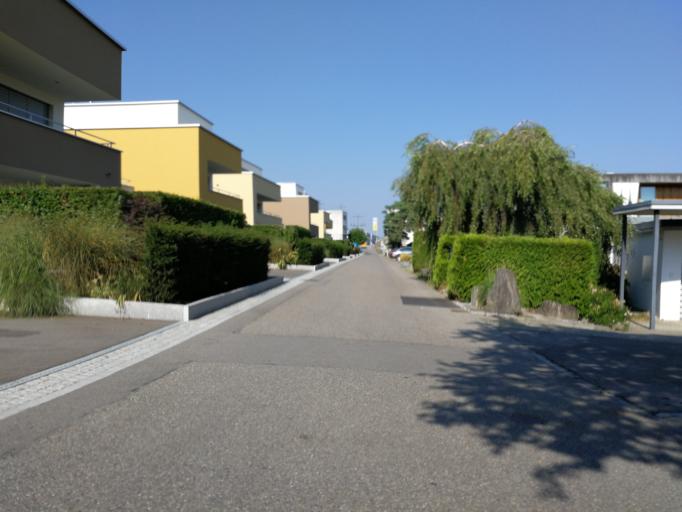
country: CH
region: Schwyz
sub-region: Bezirk March
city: Altendorf
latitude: 47.2024
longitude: 8.7990
